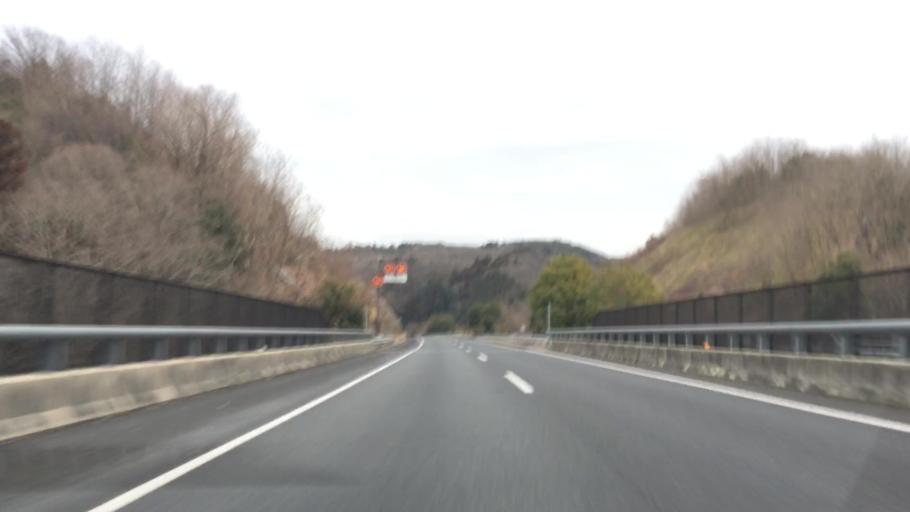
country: JP
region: Aichi
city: Seto
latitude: 35.2573
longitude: 137.1489
